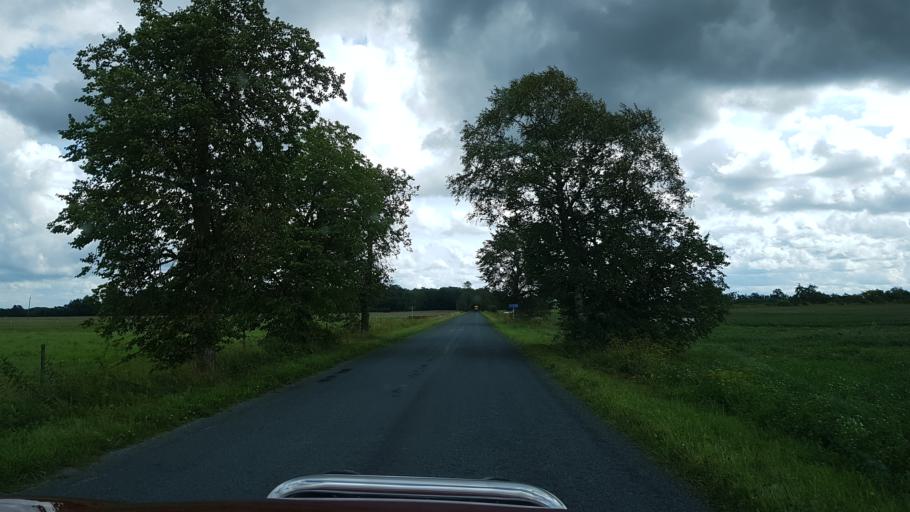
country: EE
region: Laeaene
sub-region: Lihula vald
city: Lihula
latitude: 58.7101
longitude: 24.0139
